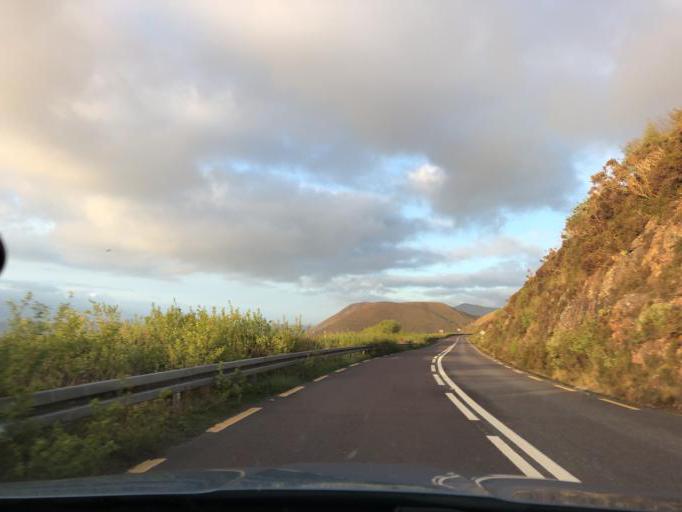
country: IE
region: Munster
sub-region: Ciarrai
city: Cahersiveen
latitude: 52.0353
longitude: -10.0410
